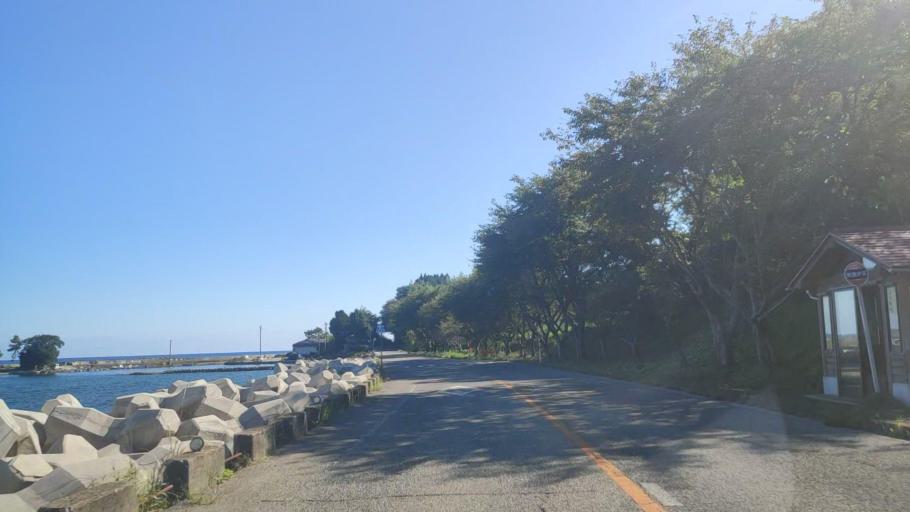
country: JP
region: Ishikawa
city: Nanao
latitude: 37.2760
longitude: 137.0967
